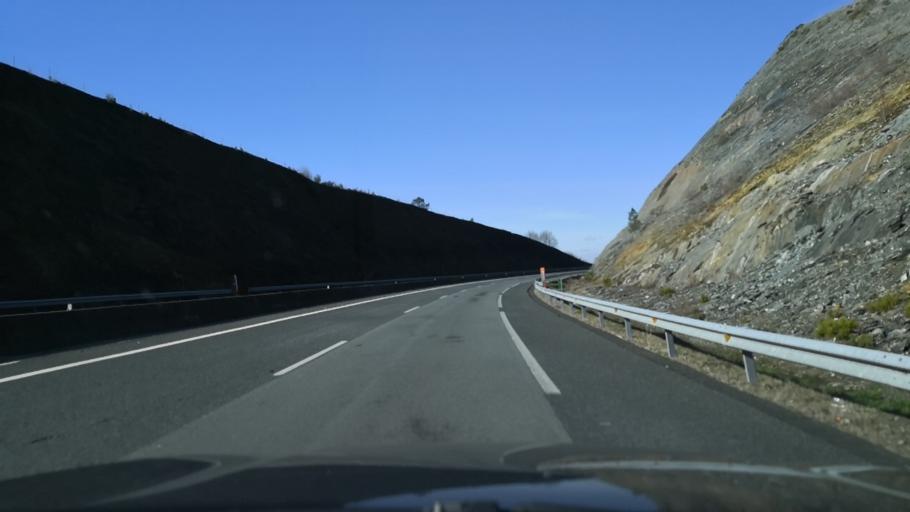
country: ES
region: Galicia
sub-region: Provincia de Pontevedra
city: Dozon
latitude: 42.5890
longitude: -8.0810
